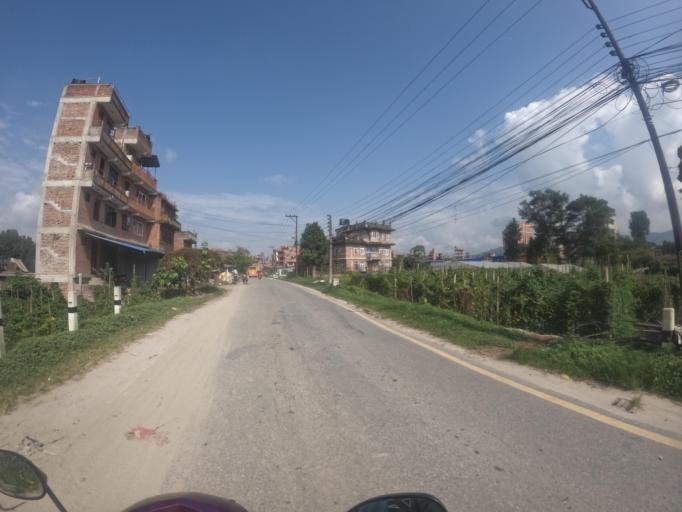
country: NP
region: Central Region
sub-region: Bagmati Zone
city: Bhaktapur
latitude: 27.6736
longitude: 85.4475
